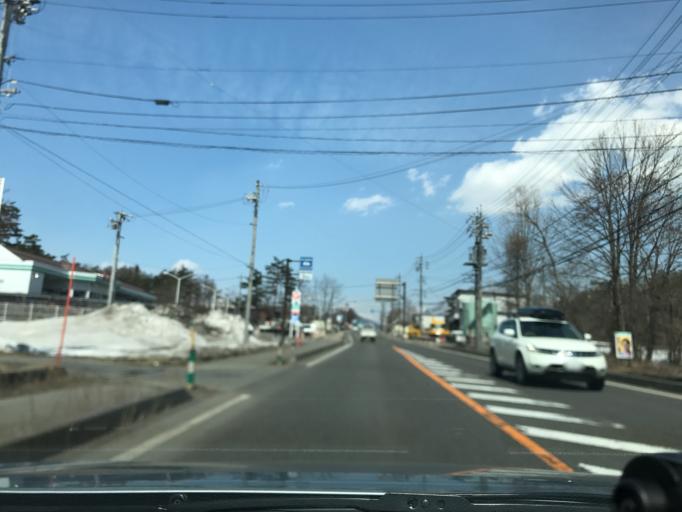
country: JP
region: Nagano
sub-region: Kitaazumi Gun
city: Hakuba
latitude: 36.6759
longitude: 137.8525
